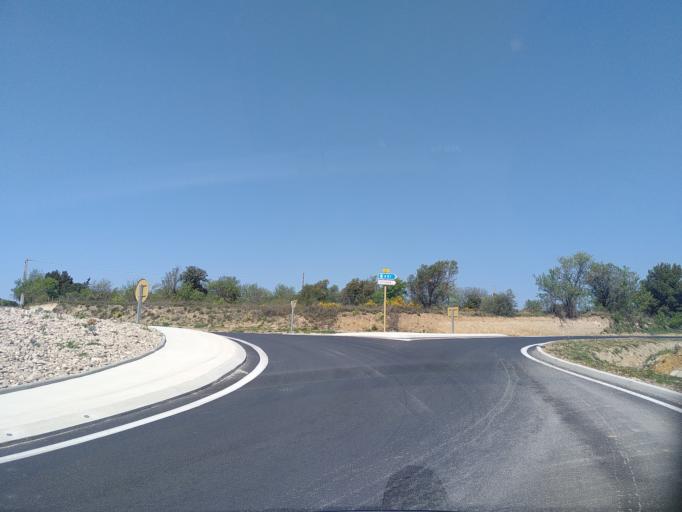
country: FR
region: Languedoc-Roussillon
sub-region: Departement de l'Aude
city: Ferrals-les-Corbieres
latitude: 43.1533
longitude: 2.7162
